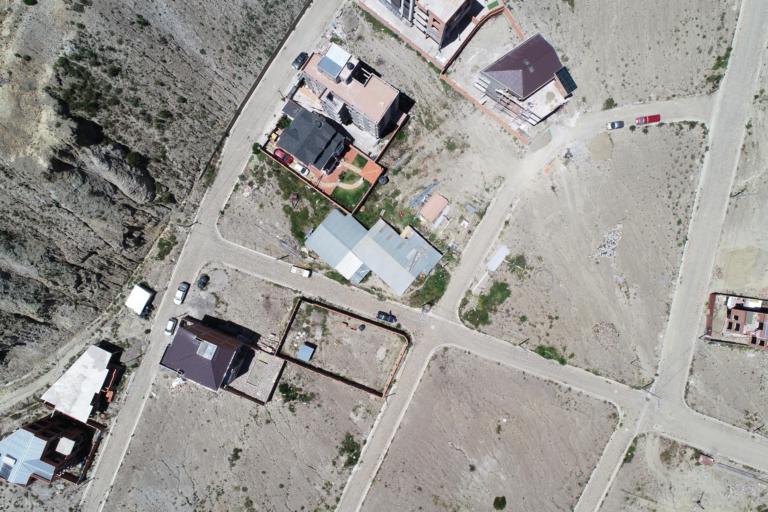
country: BO
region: La Paz
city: La Paz
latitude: -16.5223
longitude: -68.0502
